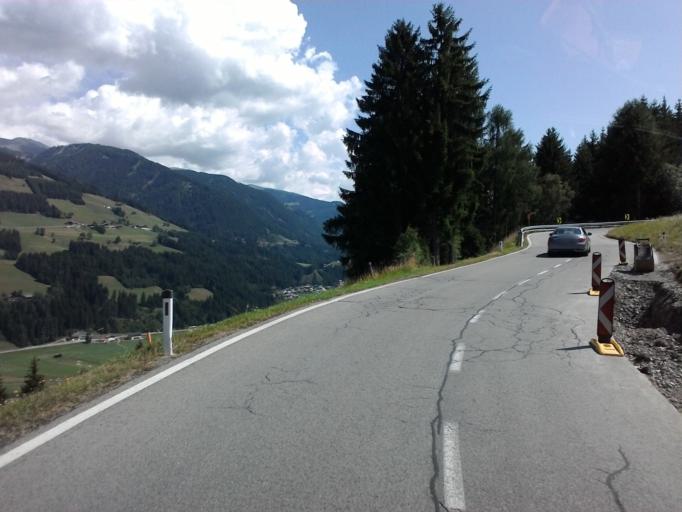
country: AT
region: Tyrol
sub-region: Politischer Bezirk Lienz
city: Strassen
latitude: 46.7405
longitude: 12.4707
